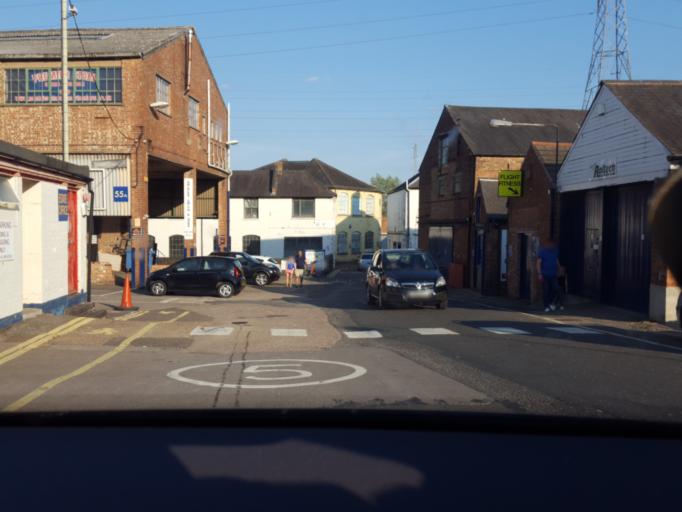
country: GB
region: England
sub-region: City of Leicester
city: Leicester
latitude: 52.6179
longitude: -1.1507
